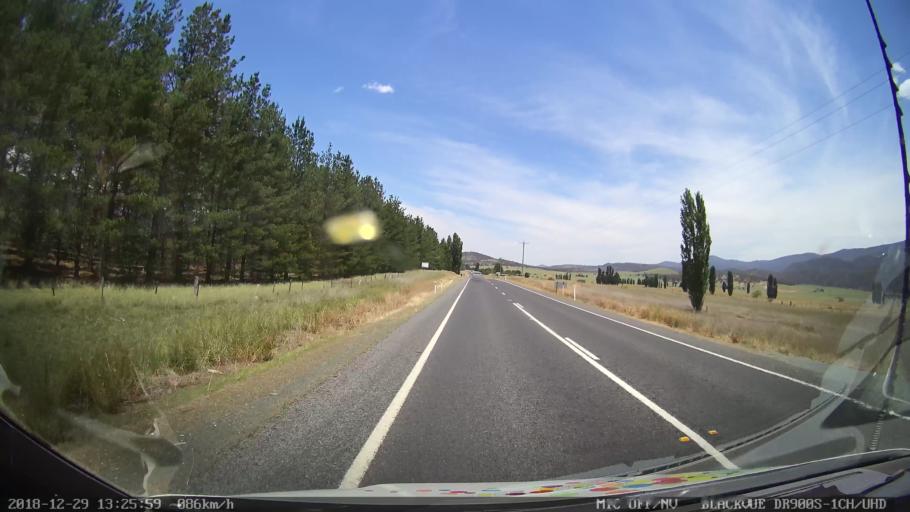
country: AU
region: New South Wales
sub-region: Cooma-Monaro
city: Cooma
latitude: -35.8496
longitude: 149.1601
